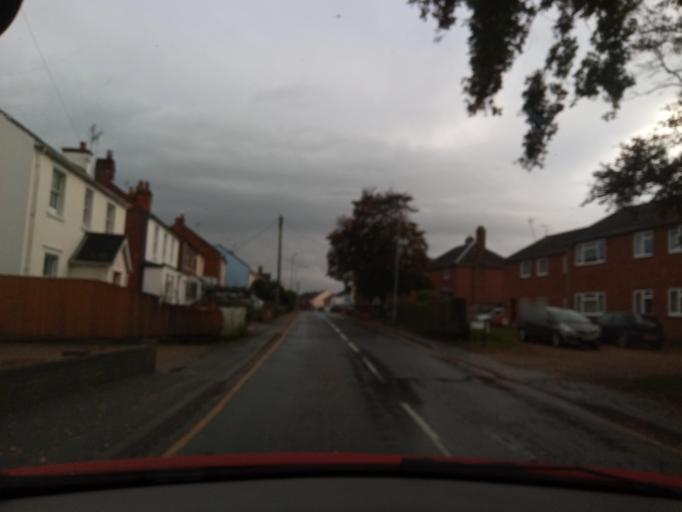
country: GB
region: England
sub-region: Essex
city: West Mersea
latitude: 51.7783
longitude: 0.9123
